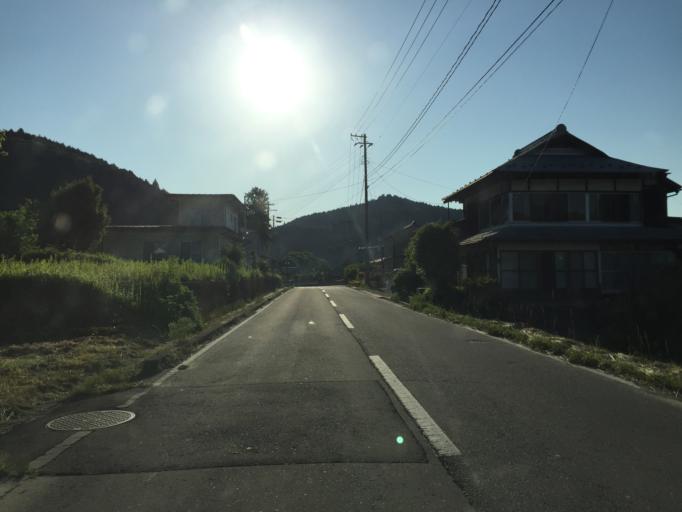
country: JP
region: Fukushima
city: Ishikawa
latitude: 36.9541
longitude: 140.4324
